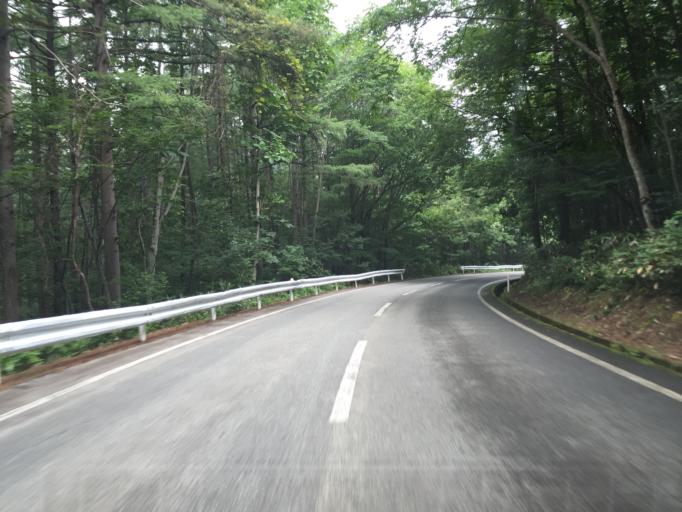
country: JP
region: Fukushima
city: Inawashiro
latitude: 37.6737
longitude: 140.1391
